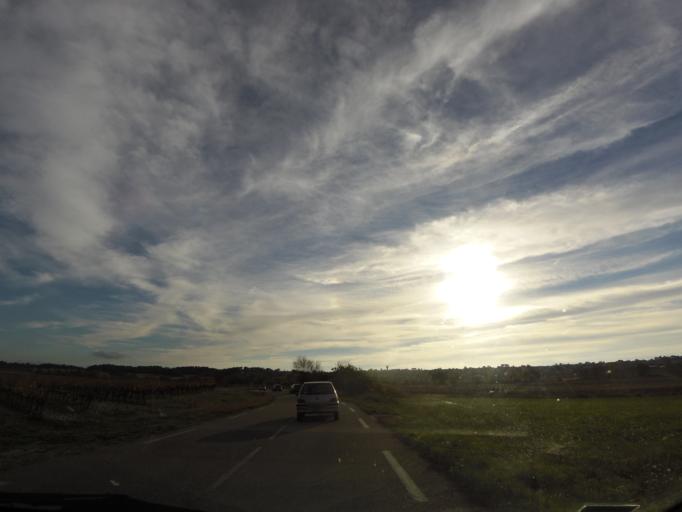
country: FR
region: Languedoc-Roussillon
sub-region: Departement du Gard
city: Ledignan
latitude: 43.9968
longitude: 4.1178
